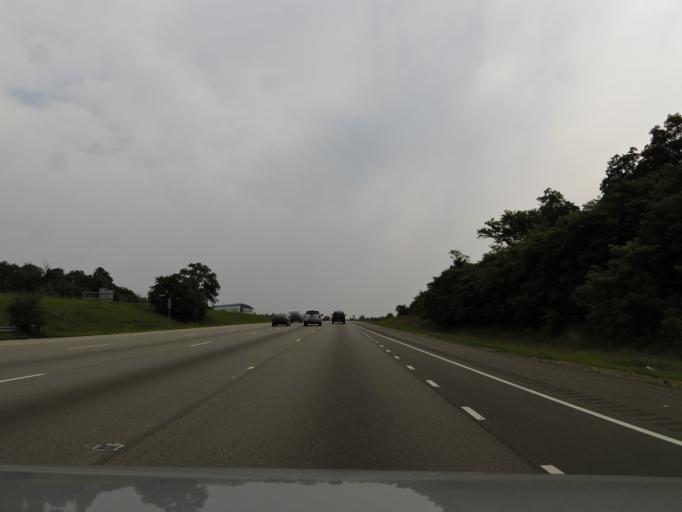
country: US
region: Ohio
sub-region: Warren County
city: Springboro
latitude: 39.5689
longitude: -84.2620
